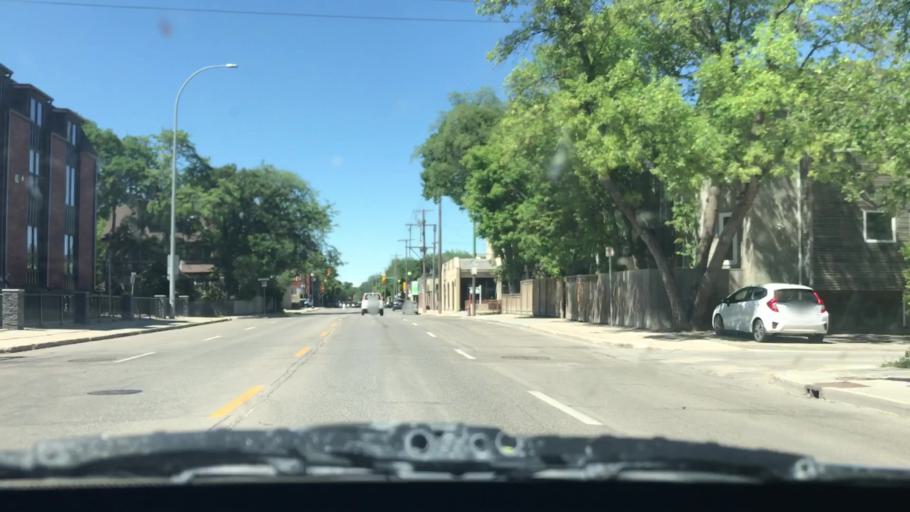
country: CA
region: Manitoba
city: Winnipeg
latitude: 49.8692
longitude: -97.1623
